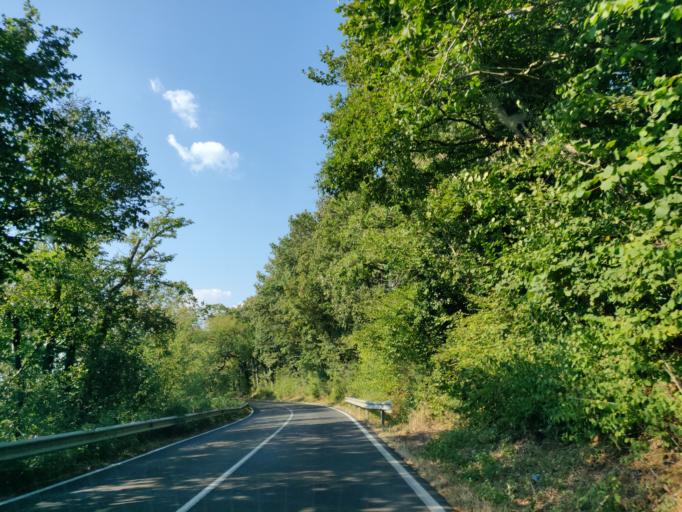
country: IT
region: Latium
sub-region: Provincia di Viterbo
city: Latera
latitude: 42.6249
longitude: 11.8377
